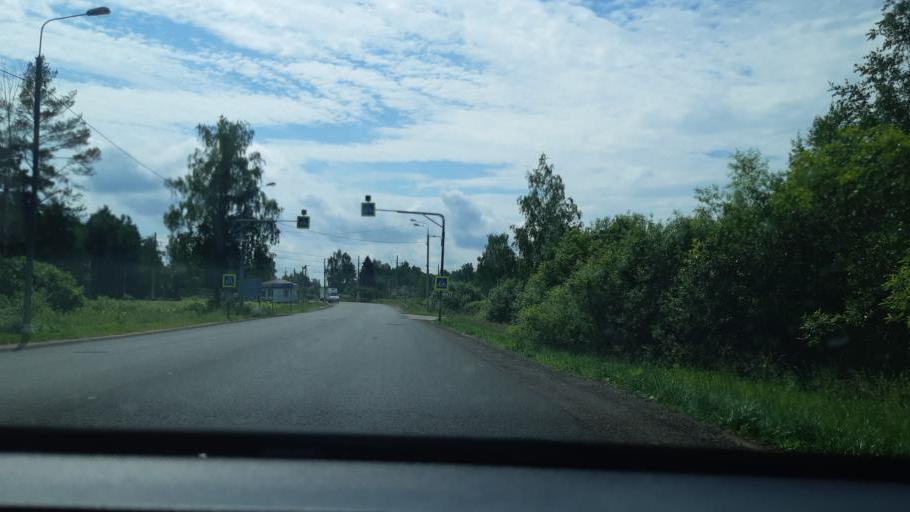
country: RU
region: Moskovskaya
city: Kubinka
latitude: 55.5948
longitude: 36.7727
